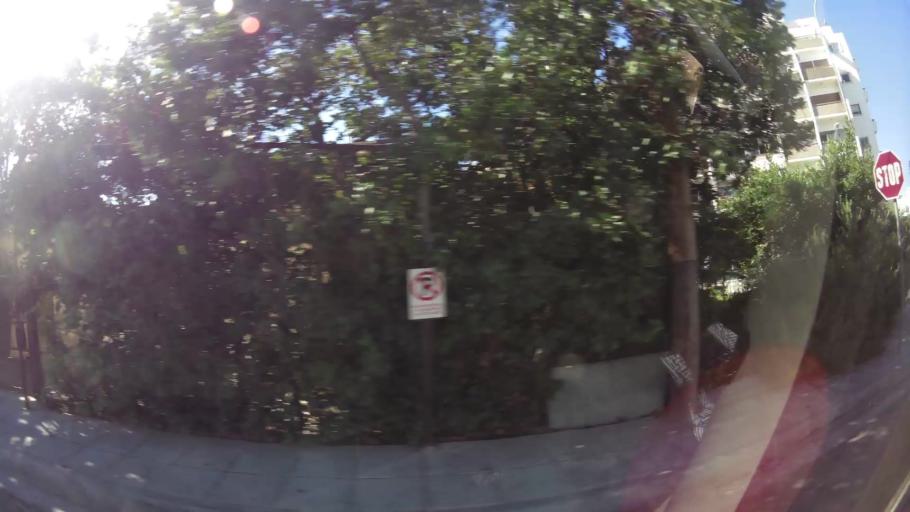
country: CY
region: Lefkosia
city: Nicosia
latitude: 35.1421
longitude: 33.3448
